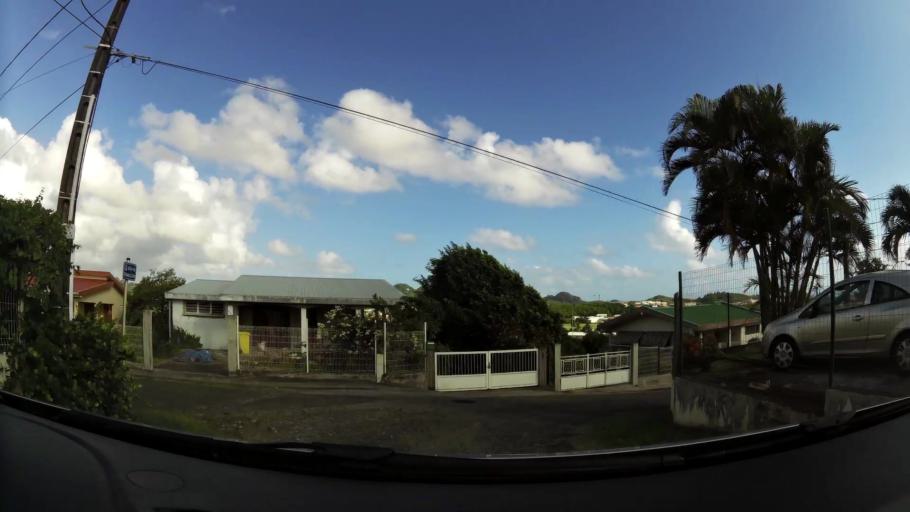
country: MQ
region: Martinique
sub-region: Martinique
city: Le Francois
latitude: 14.6132
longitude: -60.9102
